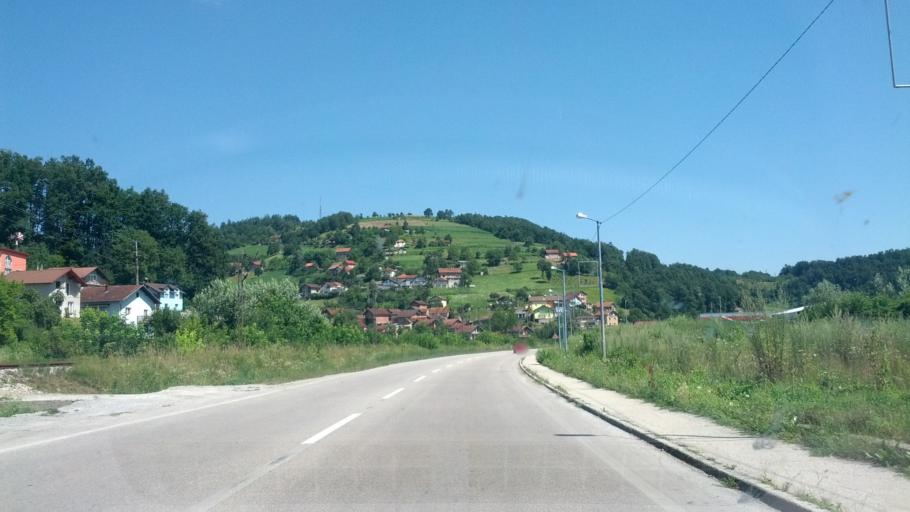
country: BA
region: Federation of Bosnia and Herzegovina
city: Bosanska Krupa
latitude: 44.8926
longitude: 16.1540
